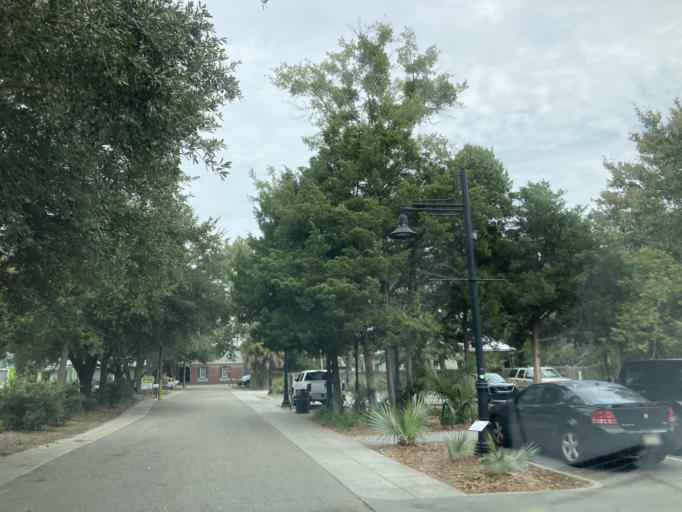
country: US
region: Mississippi
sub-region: Jackson County
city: Ocean Springs
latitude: 30.4141
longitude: -88.8263
